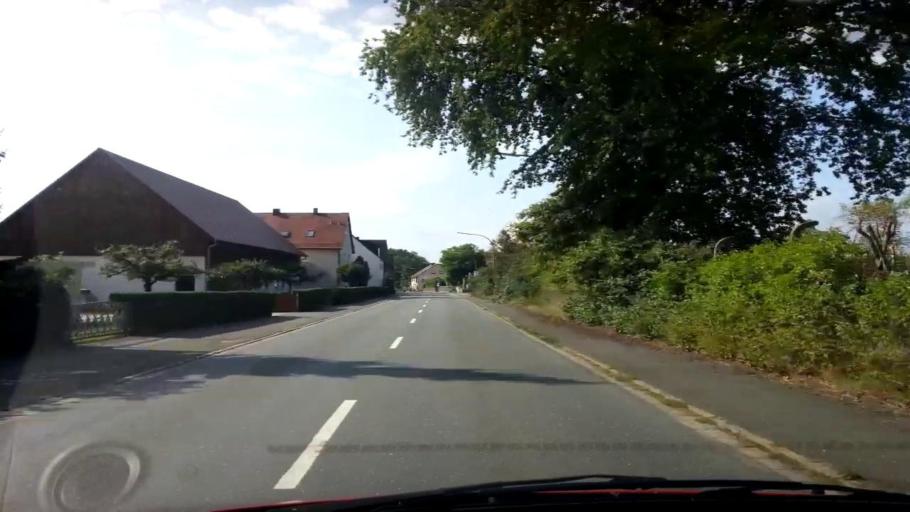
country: DE
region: Bavaria
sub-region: Upper Franconia
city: Hausen
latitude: 49.6909
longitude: 11.0359
